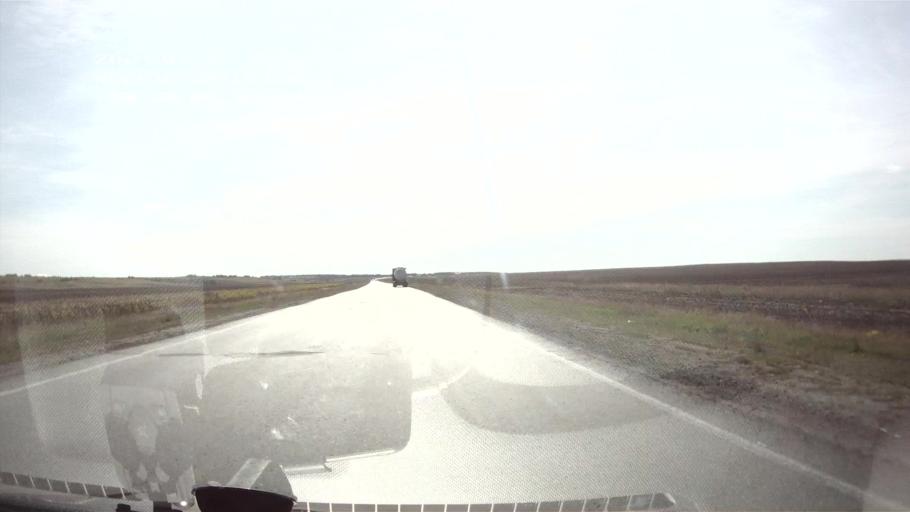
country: RU
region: Samara
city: Varlamovo
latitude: 53.0244
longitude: 48.3333
